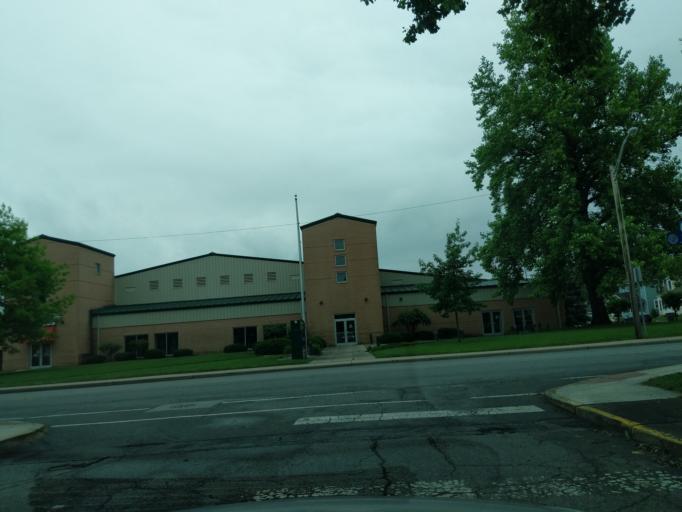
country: US
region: Indiana
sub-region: Tipton County
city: Tipton
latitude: 40.2823
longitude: -86.0462
